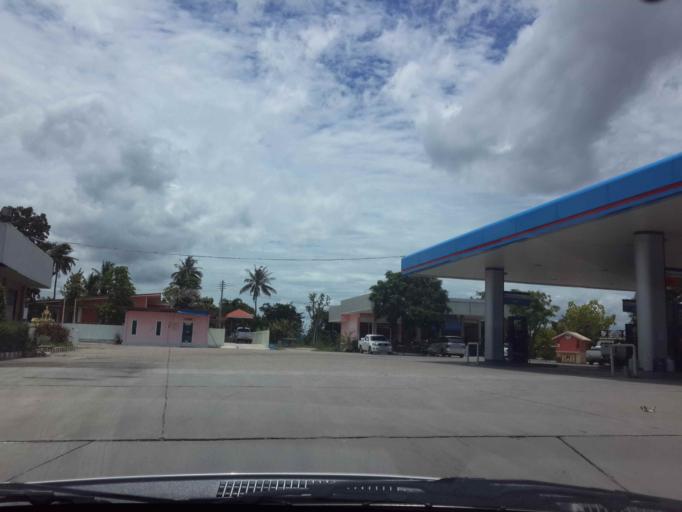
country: TH
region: Prachuap Khiri Khan
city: Hua Hin
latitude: 12.6713
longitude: 99.9522
